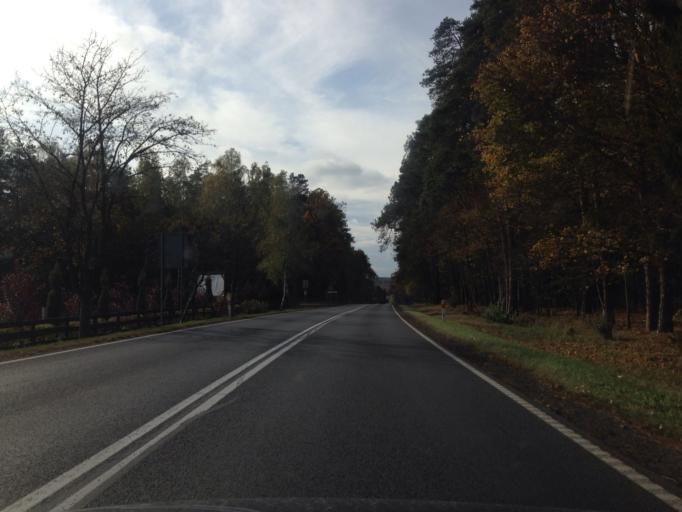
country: PL
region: Kujawsko-Pomorskie
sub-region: Powiat brodnicki
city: Brodnica
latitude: 53.2861
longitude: 19.4874
